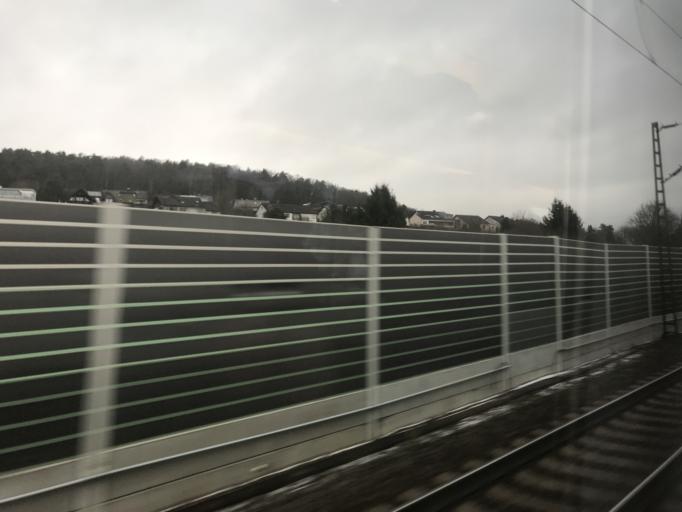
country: DE
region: Hesse
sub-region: Regierungsbezirk Kassel
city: Petersberg
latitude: 50.5822
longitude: 9.7264
